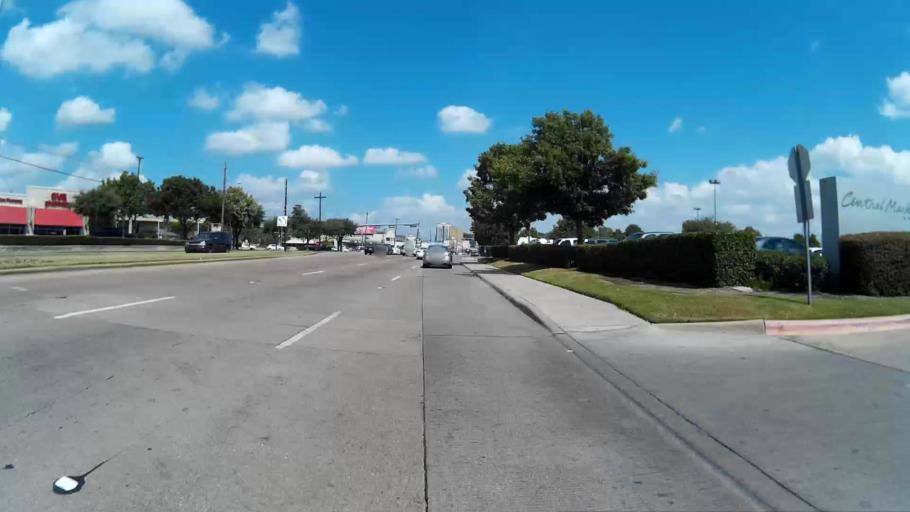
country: US
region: Texas
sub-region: Dallas County
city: Highland Park
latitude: 32.8498
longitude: -96.7700
